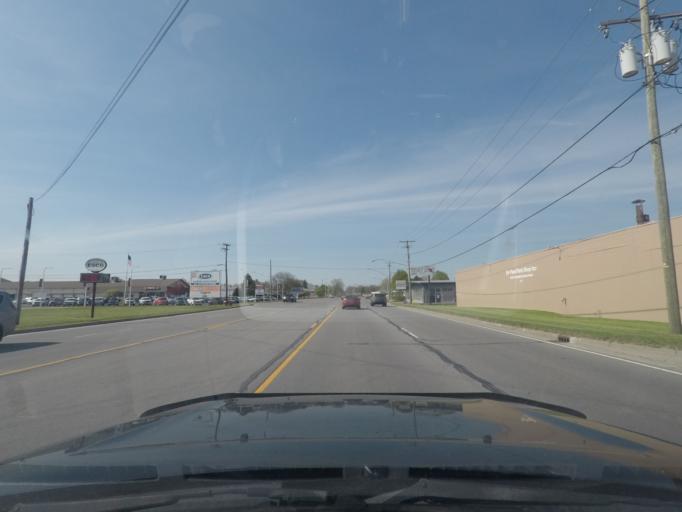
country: US
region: Indiana
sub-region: Elkhart County
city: Elkhart
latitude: 41.6979
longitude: -86.0036
